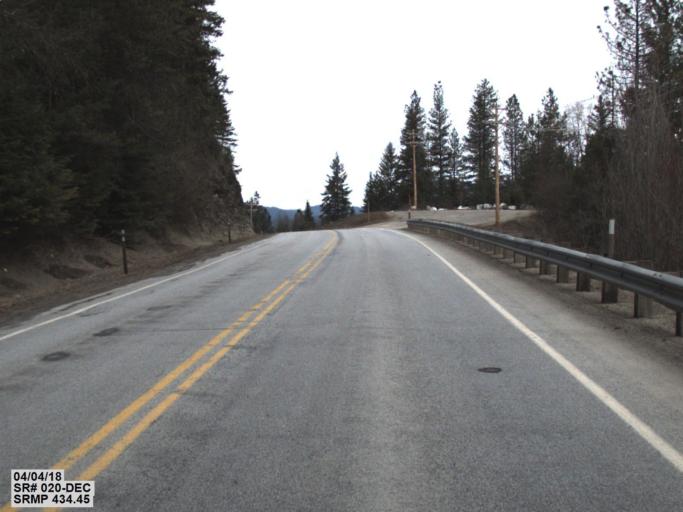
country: US
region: Washington
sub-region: Pend Oreille County
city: Newport
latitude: 48.2131
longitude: -117.0698
